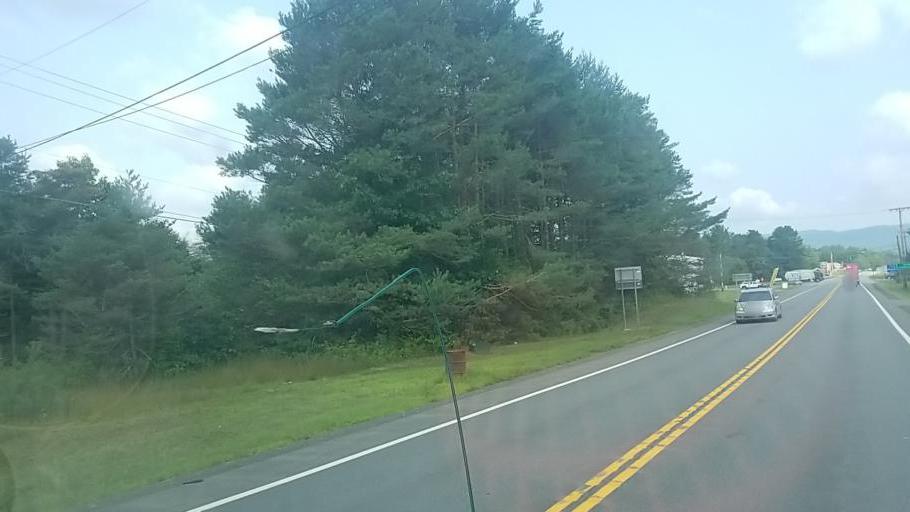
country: US
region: New York
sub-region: Fulton County
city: Broadalbin
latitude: 43.0753
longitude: -74.2576
